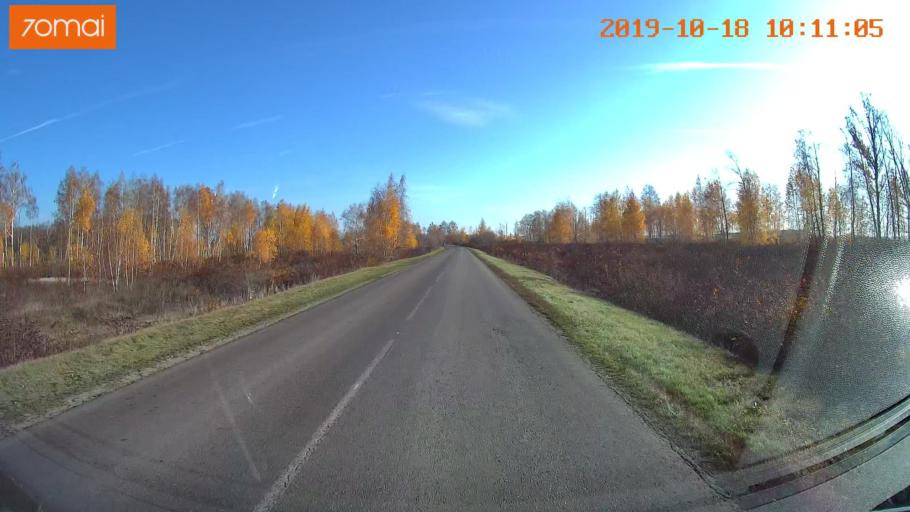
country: RU
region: Tula
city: Kurkino
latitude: 53.3807
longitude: 38.4908
